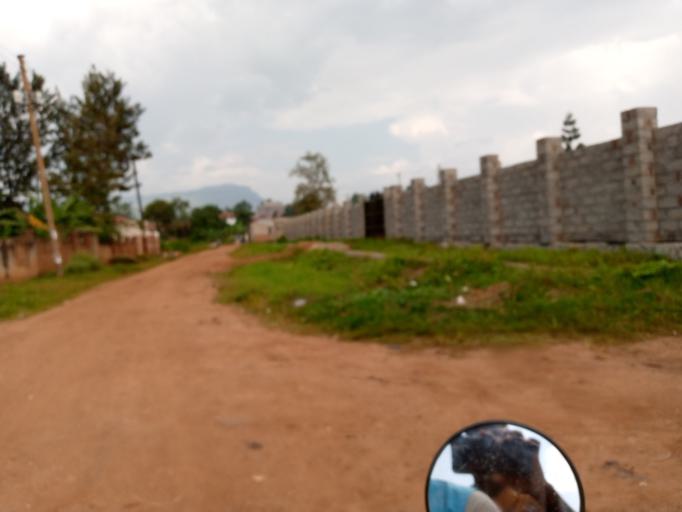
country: UG
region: Eastern Region
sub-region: Mbale District
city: Mbale
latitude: 1.0846
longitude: 34.1612
